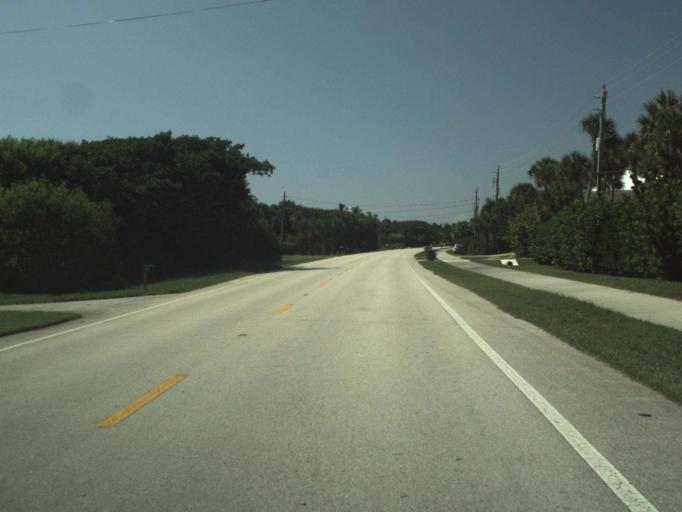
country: US
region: Florida
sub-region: Indian River County
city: Sebastian
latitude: 27.8247
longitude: -80.4297
